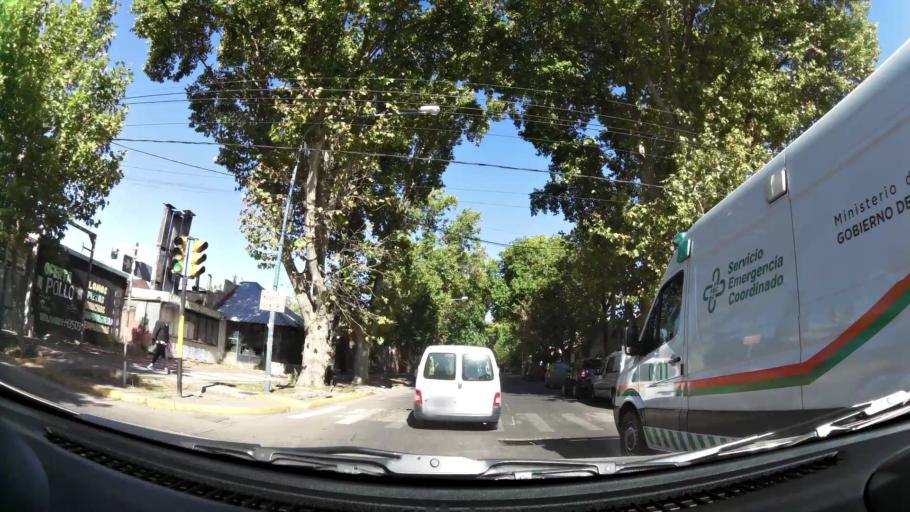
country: AR
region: Mendoza
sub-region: Departamento de Godoy Cruz
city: Godoy Cruz
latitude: -32.9244
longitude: -68.8594
